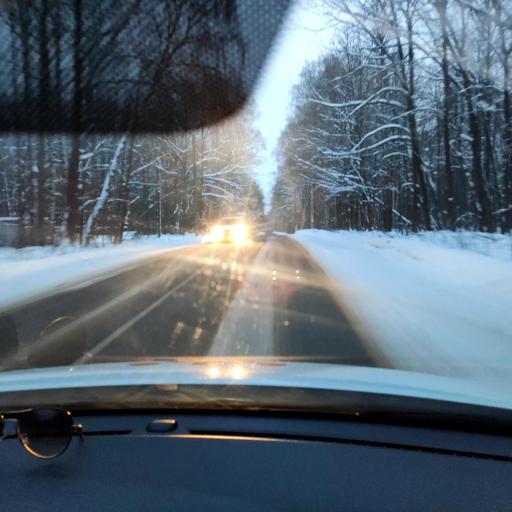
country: RU
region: Tatarstan
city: Vysokaya Gora
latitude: 55.9341
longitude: 49.1801
